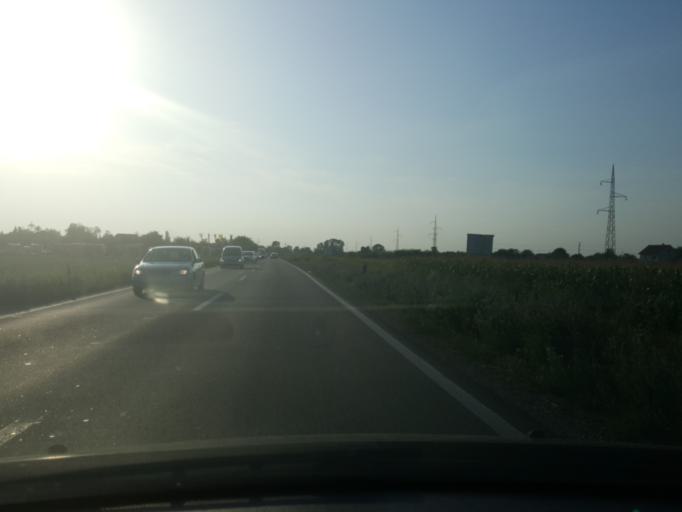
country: RS
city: Majur
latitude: 44.7644
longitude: 19.6368
